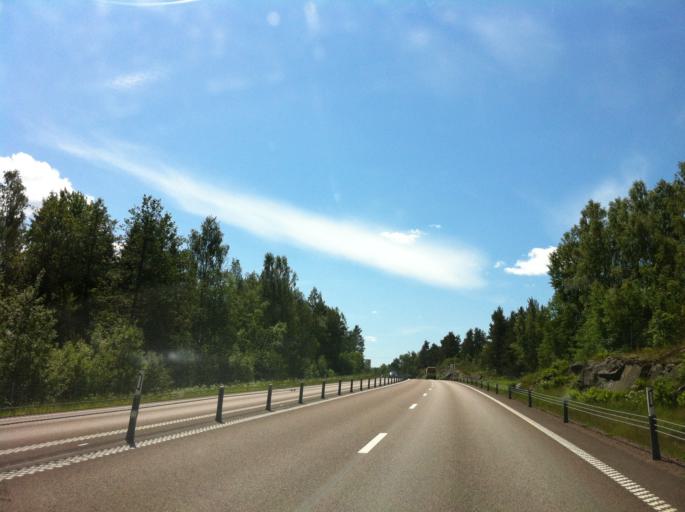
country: SE
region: Vaestra Goetaland
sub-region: Melleruds Kommun
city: Mellerud
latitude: 58.8224
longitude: 12.5237
